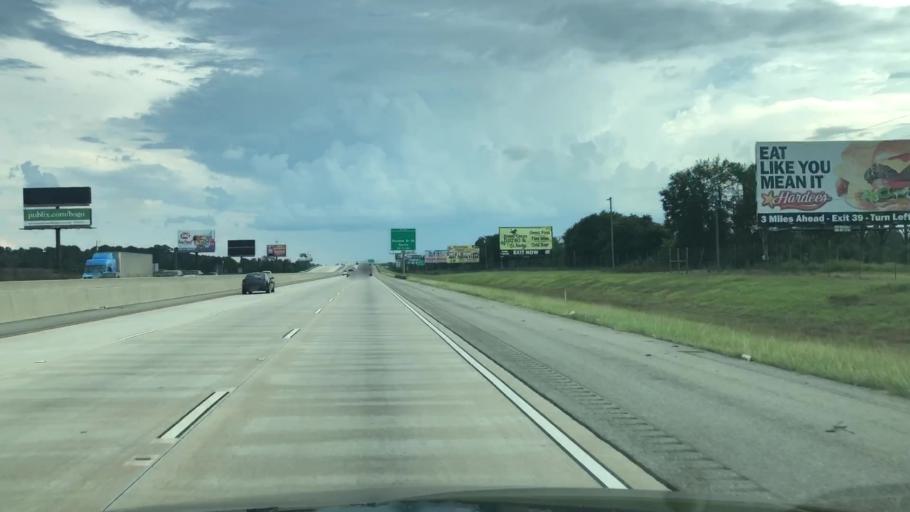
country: US
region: Georgia
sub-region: Cook County
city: Sparks
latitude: 31.1778
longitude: -83.4523
